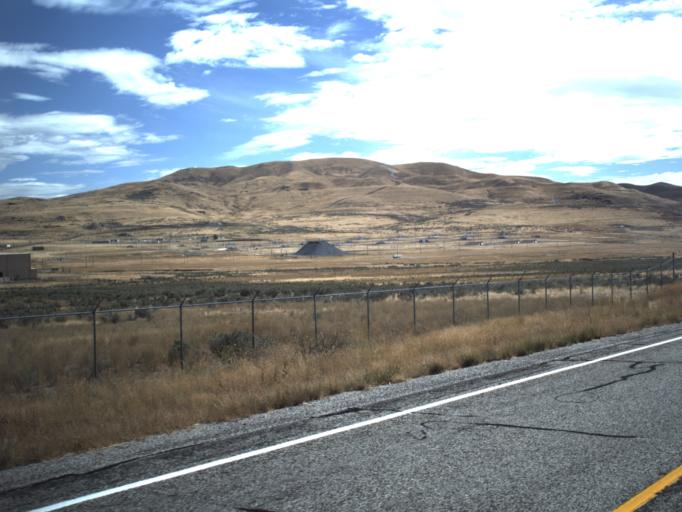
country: US
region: Utah
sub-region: Box Elder County
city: Tremonton
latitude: 41.7084
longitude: -112.4512
